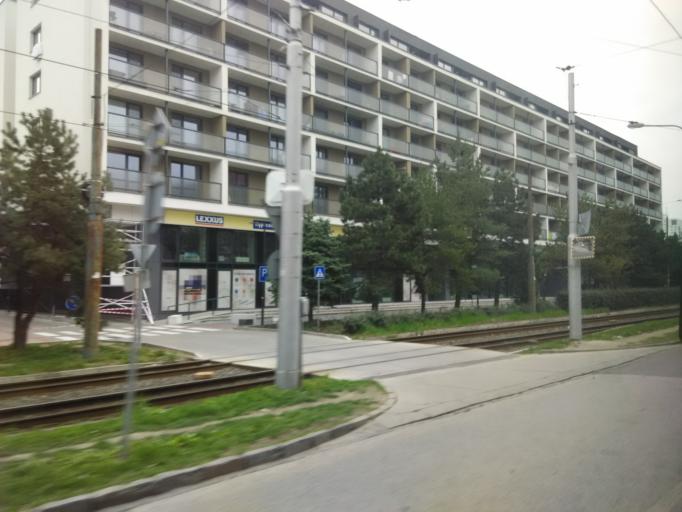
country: SK
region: Bratislavsky
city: Bratislava
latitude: 48.1571
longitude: 17.1316
